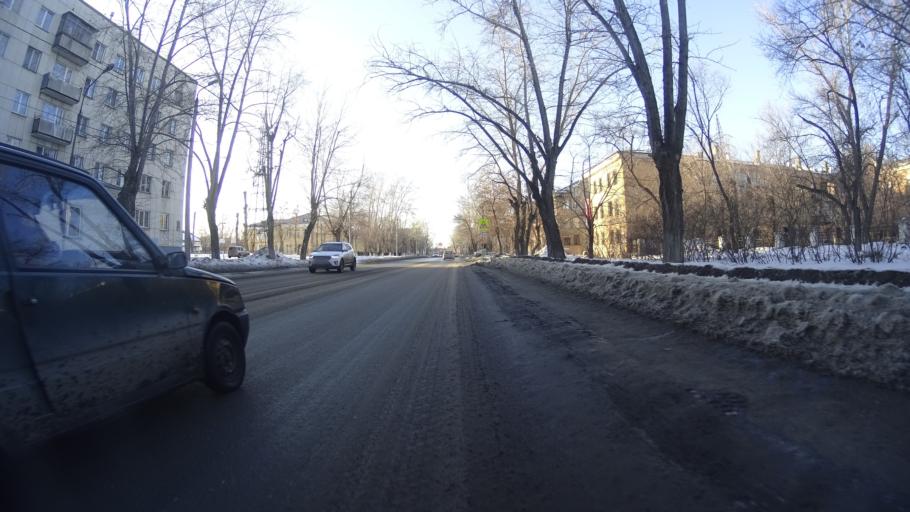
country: RU
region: Chelyabinsk
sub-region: Gorod Chelyabinsk
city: Chelyabinsk
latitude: 55.1290
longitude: 61.4670
